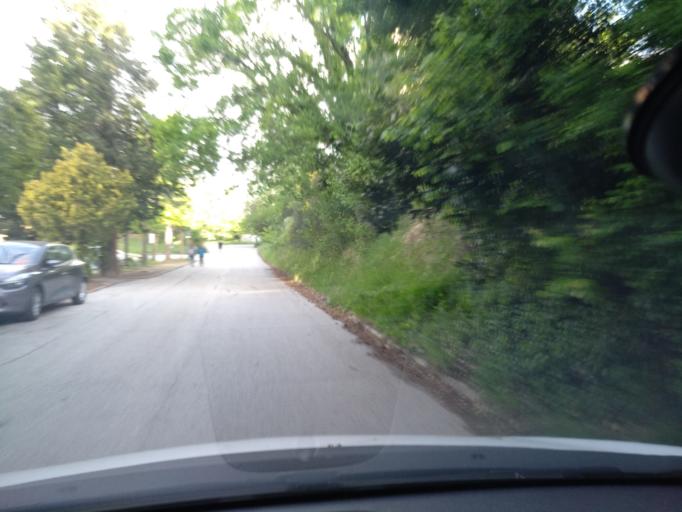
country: IT
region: The Marches
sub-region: Provincia di Pesaro e Urbino
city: Urbino
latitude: 43.7365
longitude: 12.6298
